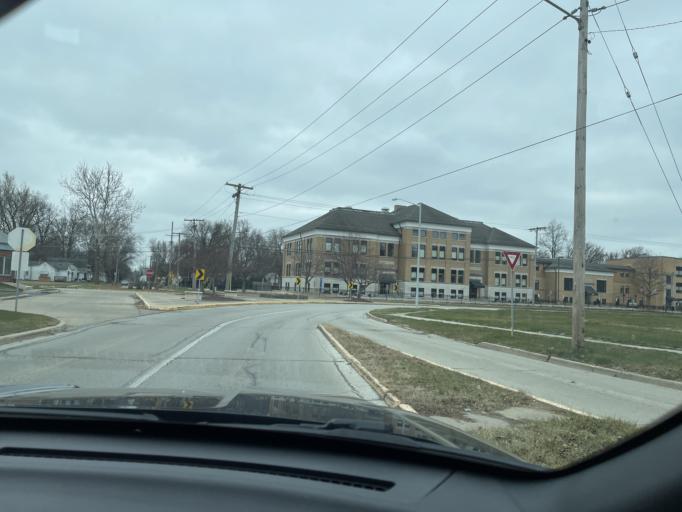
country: US
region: Illinois
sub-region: Sangamon County
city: Springfield
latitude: 39.7947
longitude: -89.6585
